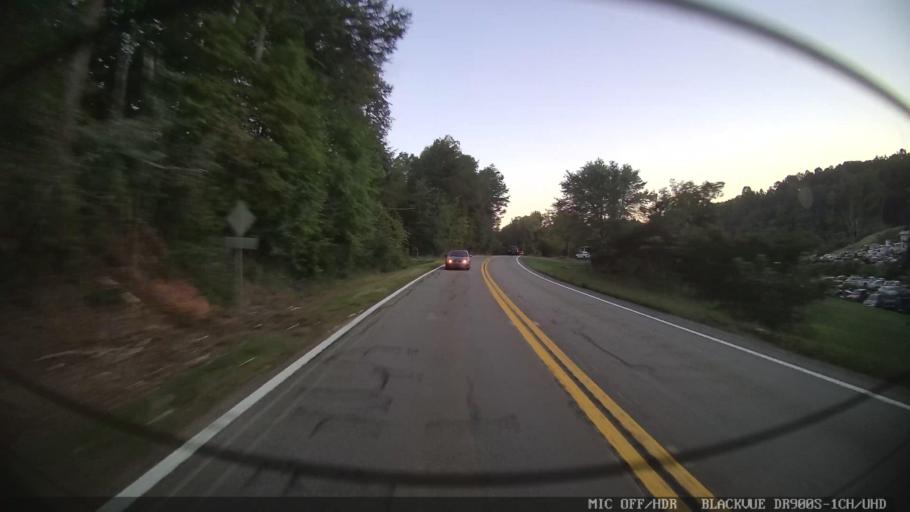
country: US
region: Georgia
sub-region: Gilmer County
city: Ellijay
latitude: 34.7188
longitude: -84.5026
